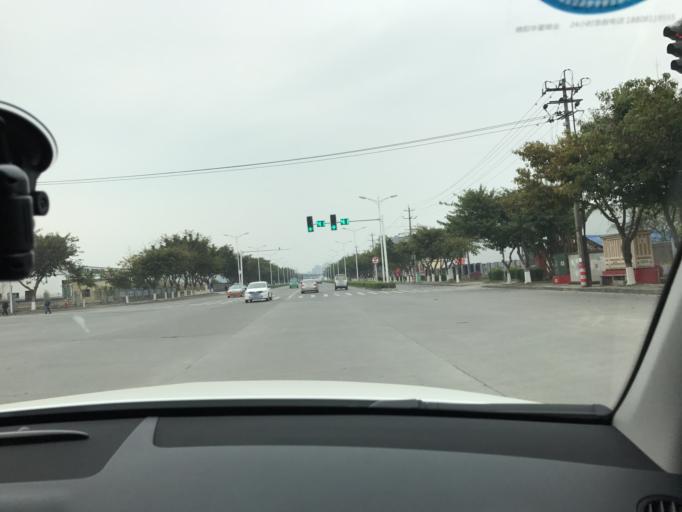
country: CN
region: Sichuan
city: Mianyang
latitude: 31.4587
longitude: 104.6813
